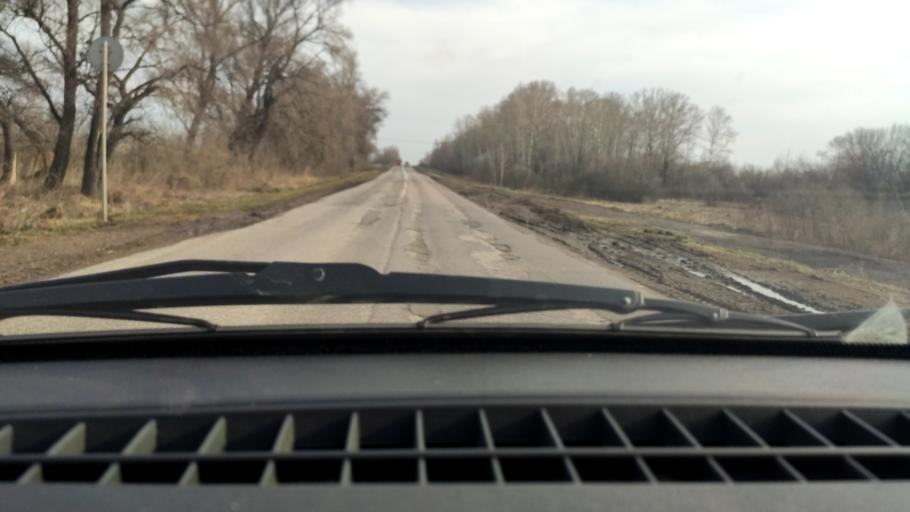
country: RU
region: Bashkortostan
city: Chishmy
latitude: 54.5131
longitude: 55.2932
